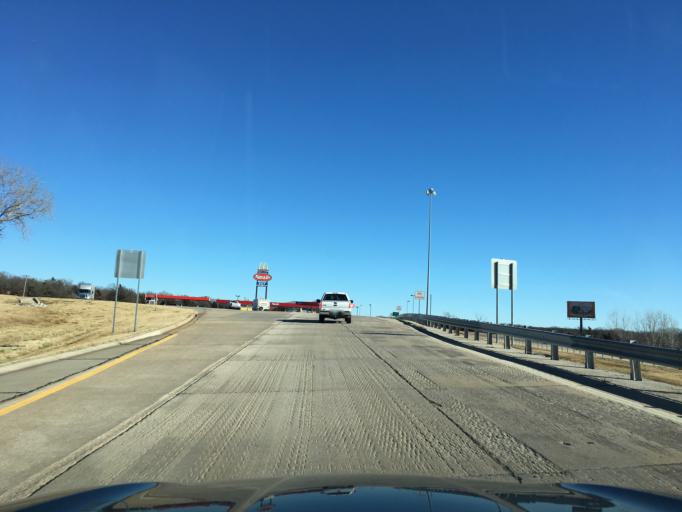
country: US
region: Oklahoma
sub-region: Pawnee County
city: Pawnee
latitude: 36.2244
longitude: -96.7987
